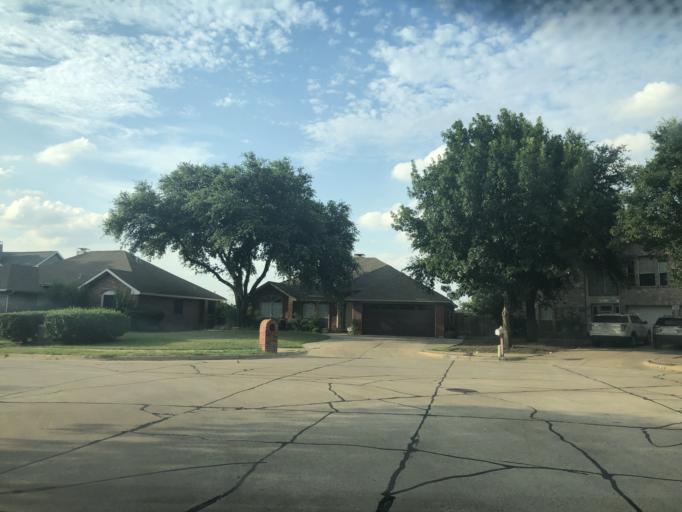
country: US
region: Texas
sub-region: Dallas County
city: Irving
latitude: 32.7894
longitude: -96.9659
